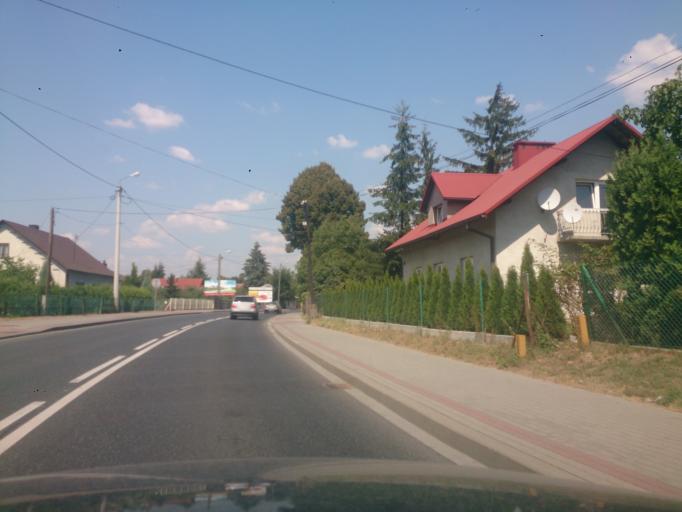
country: PL
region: Subcarpathian Voivodeship
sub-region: Powiat kolbuszowski
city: Kolbuszowa
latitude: 50.2382
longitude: 21.7803
